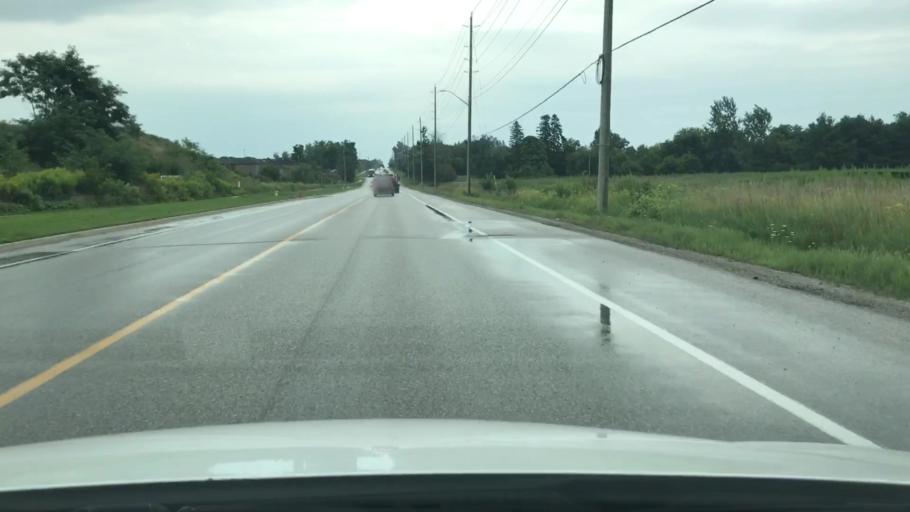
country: CA
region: Ontario
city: Innisfil
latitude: 44.3501
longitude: -79.6203
